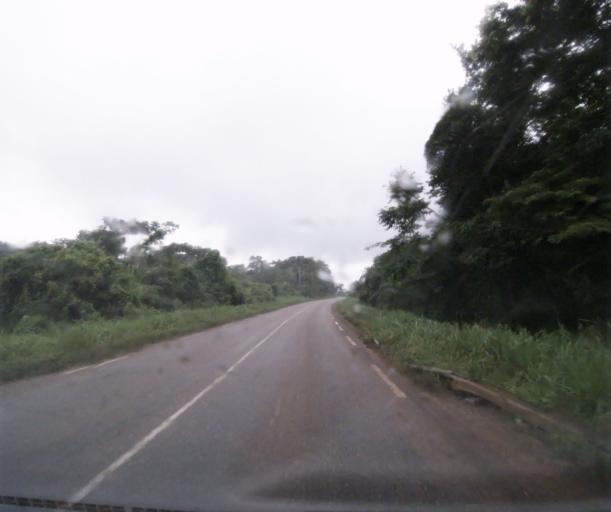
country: CM
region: Centre
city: Eseka
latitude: 3.8699
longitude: 10.6496
